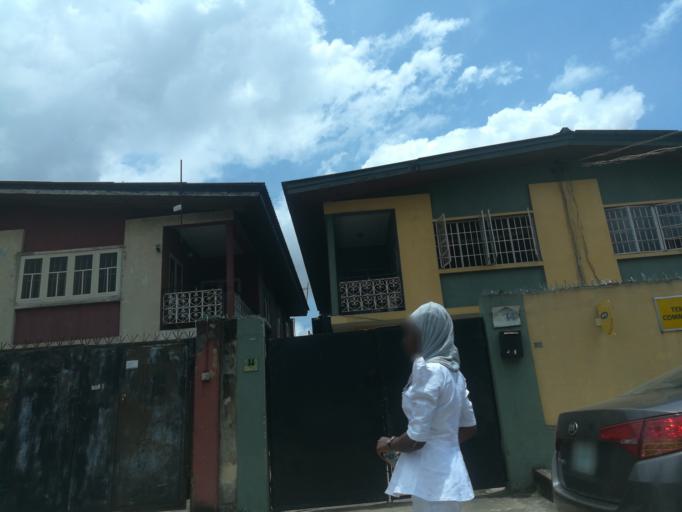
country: NG
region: Lagos
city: Somolu
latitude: 6.5483
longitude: 3.3589
